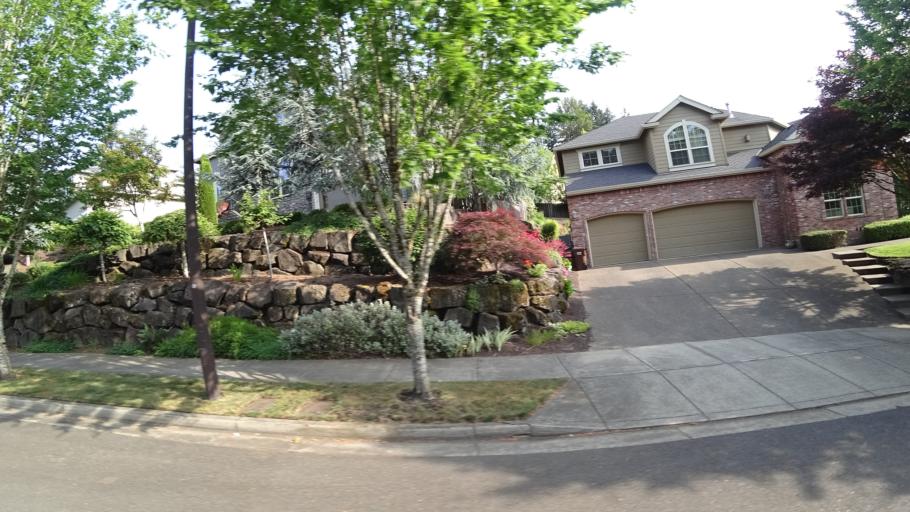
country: US
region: Oregon
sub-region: Clackamas County
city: Happy Valley
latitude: 45.4524
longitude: -122.5305
